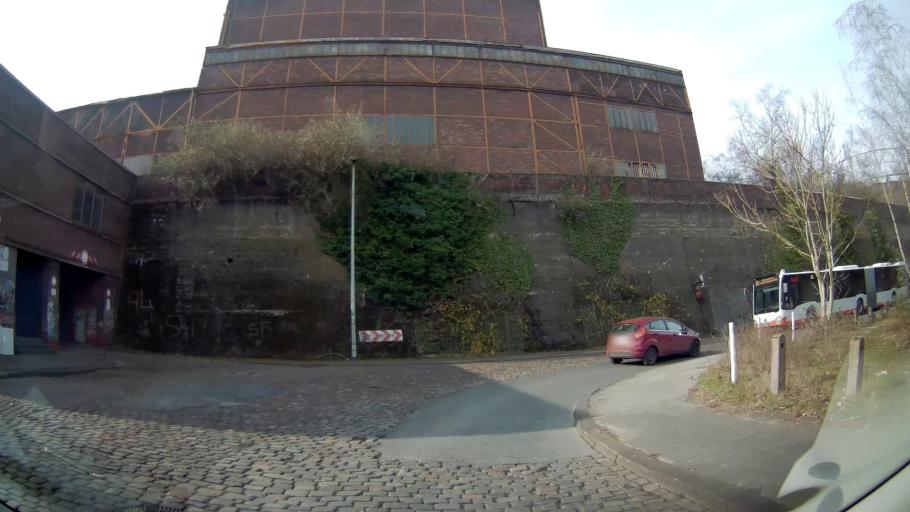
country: DE
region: North Rhine-Westphalia
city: Meiderich
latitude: 51.4652
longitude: 6.7397
